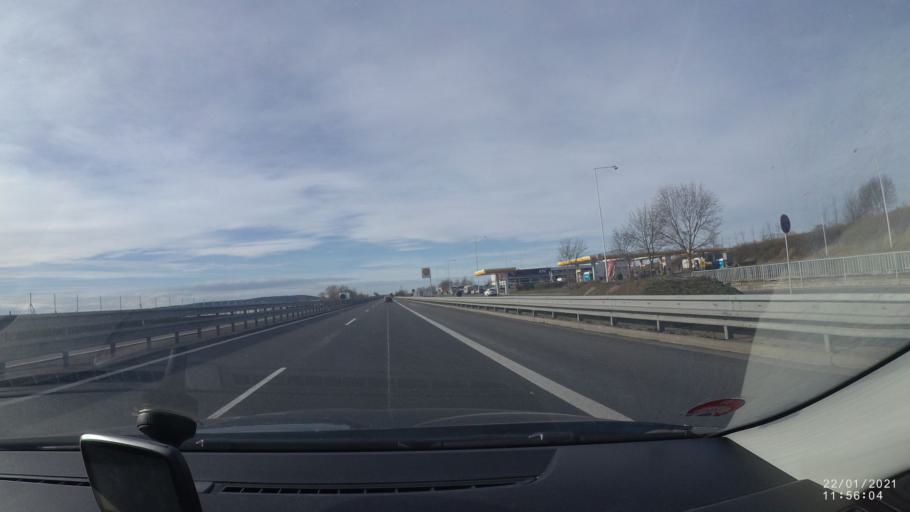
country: CZ
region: Plzensky
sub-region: Okres Rokycany
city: Rokycany
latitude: 49.7576
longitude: 13.6183
